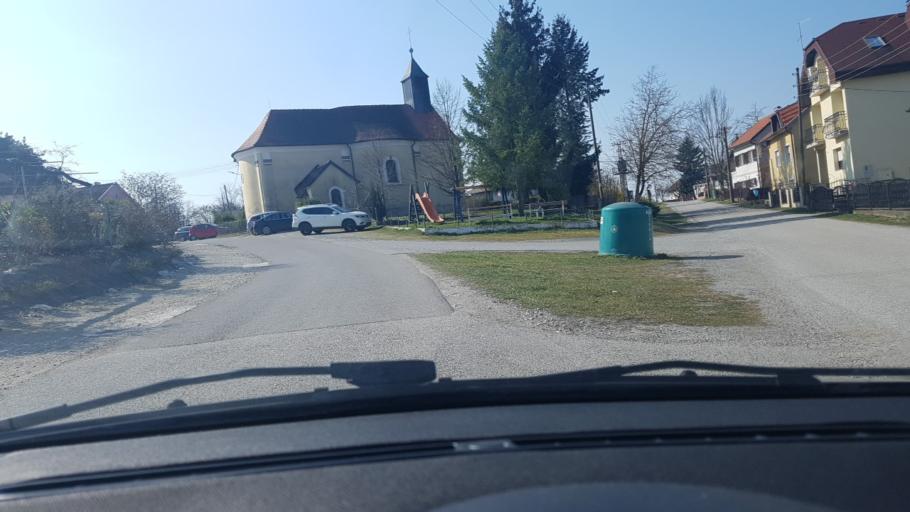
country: HR
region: Krapinsko-Zagorska
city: Oroslavje
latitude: 45.9808
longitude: 15.8964
